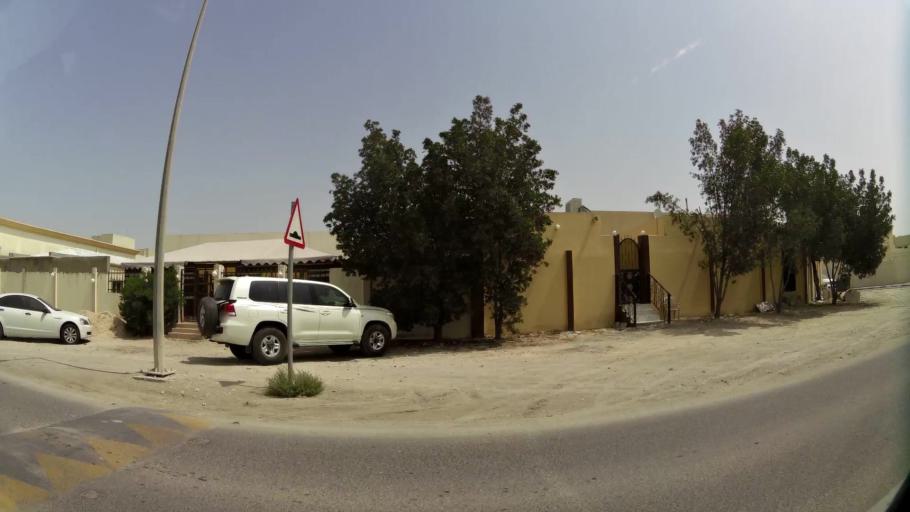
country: QA
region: Baladiyat ar Rayyan
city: Ar Rayyan
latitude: 25.2465
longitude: 51.4245
